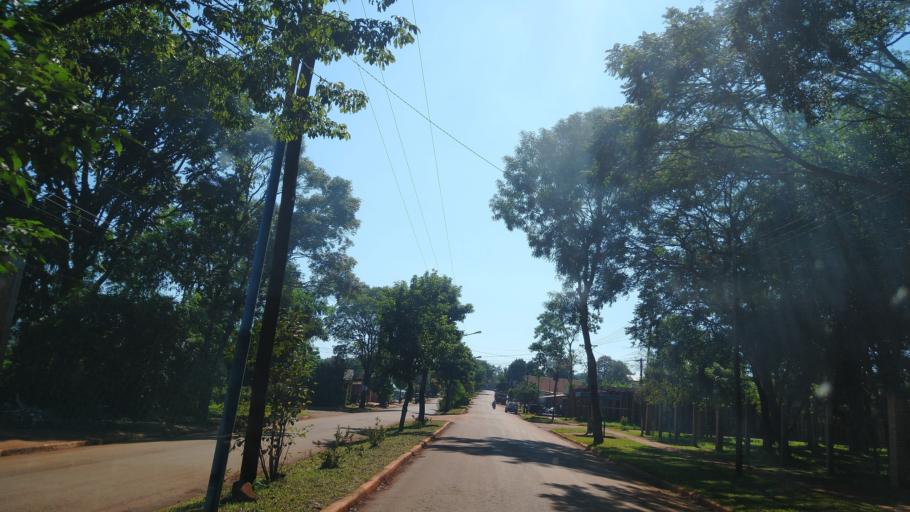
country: AR
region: Misiones
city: Puerto Libertad
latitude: -25.9766
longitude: -54.5709
